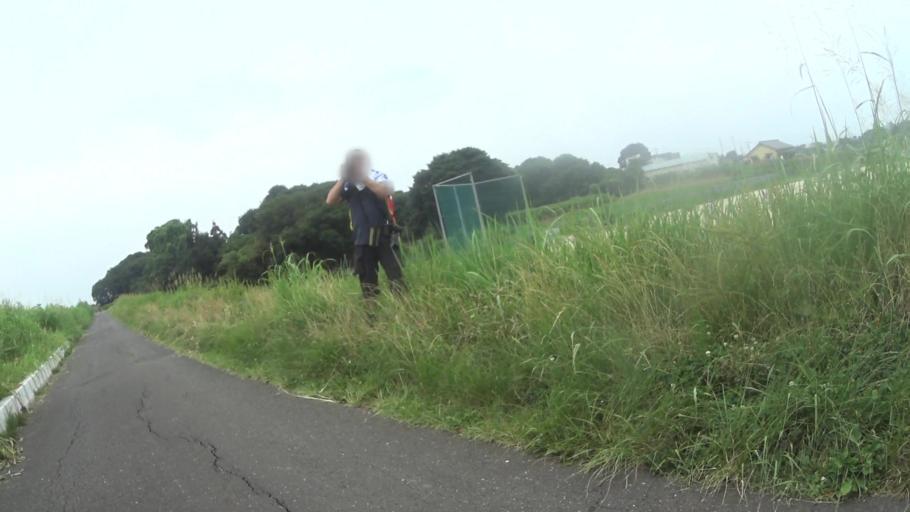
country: JP
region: Saitama
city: Okegawa
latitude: 35.9387
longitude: 139.5508
